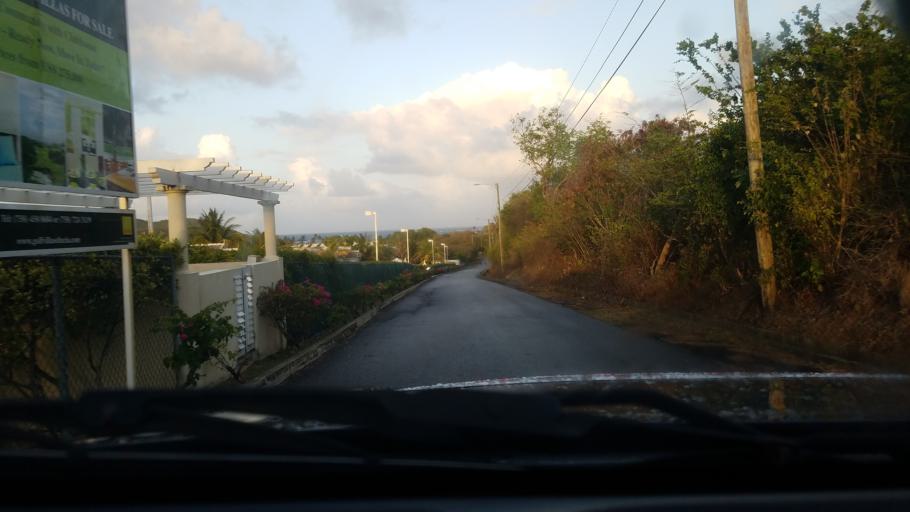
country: LC
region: Gros-Islet
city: Gros Islet
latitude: 14.0899
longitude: -60.9352
